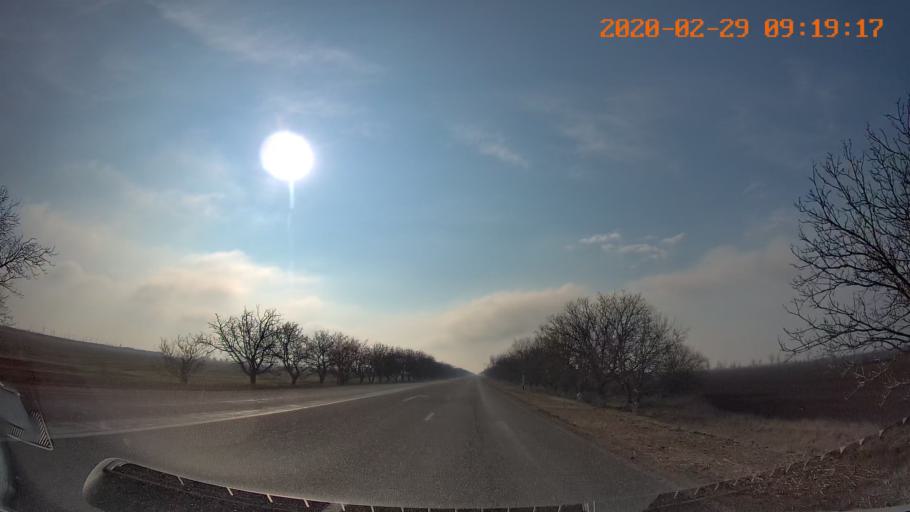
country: MD
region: Telenesti
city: Pervomaisc
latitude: 46.7649
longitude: 29.9375
